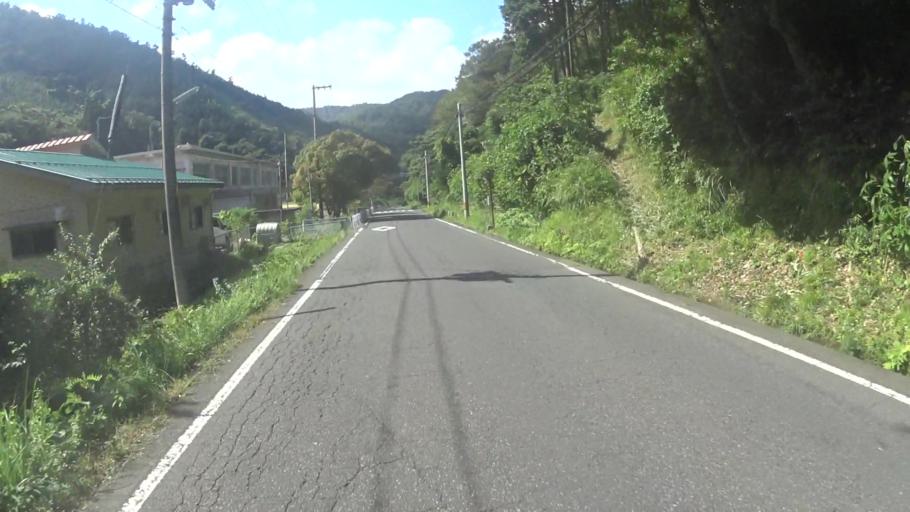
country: JP
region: Kyoto
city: Miyazu
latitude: 35.6875
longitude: 135.2826
